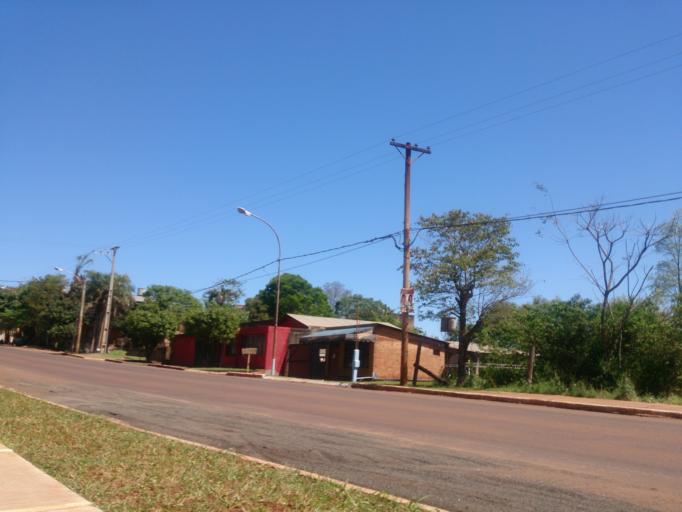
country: AR
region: Misiones
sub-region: Departamento de Obera
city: Obera
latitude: -27.4972
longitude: -55.1131
